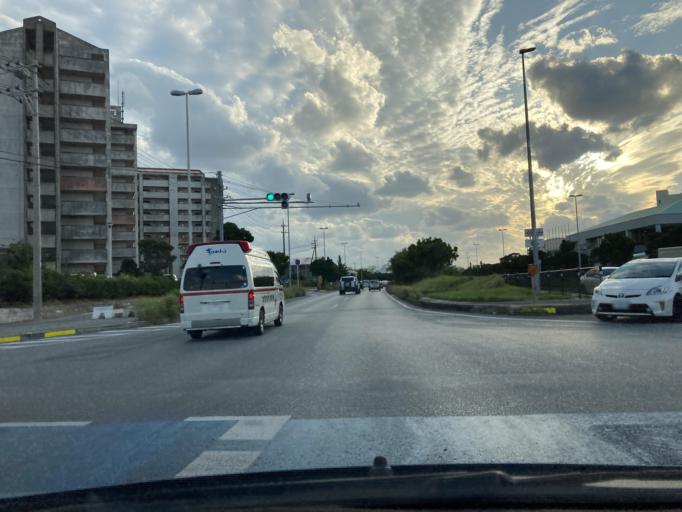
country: JP
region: Okinawa
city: Ginowan
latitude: 26.2818
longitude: 127.7426
